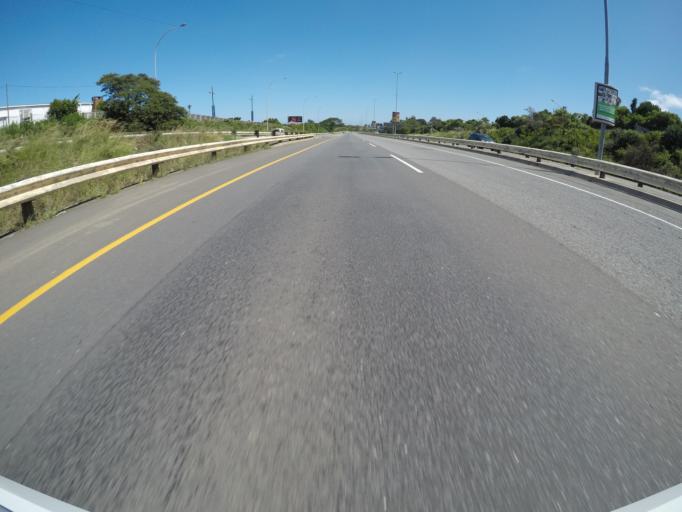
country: ZA
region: Eastern Cape
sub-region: Buffalo City Metropolitan Municipality
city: East London
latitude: -32.9944
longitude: 27.9178
